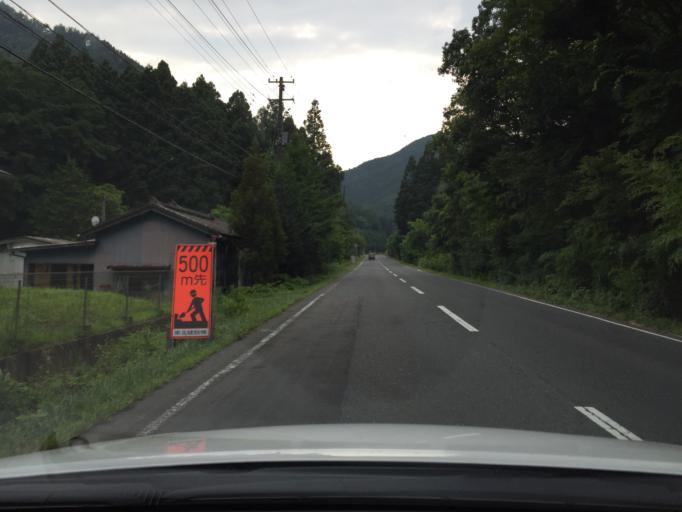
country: JP
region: Fukushima
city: Namie
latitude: 37.6652
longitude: 140.8744
